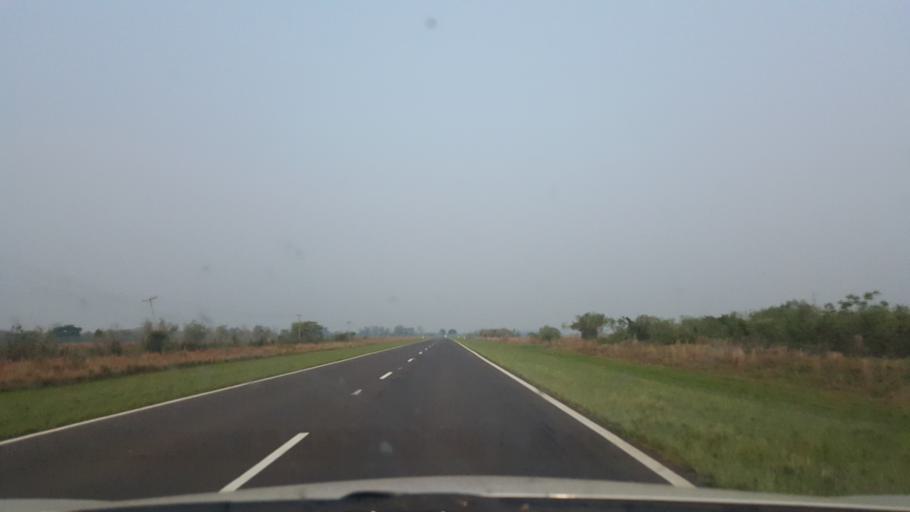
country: AR
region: Corrientes
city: Ita Ibate
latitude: -27.4632
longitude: -57.3130
